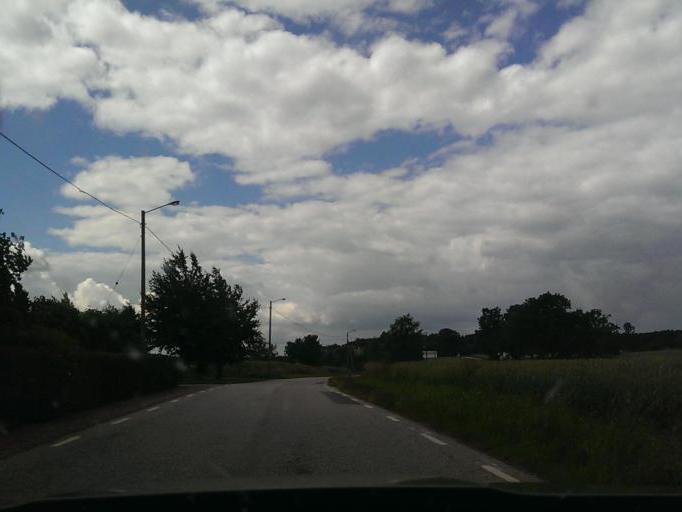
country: SE
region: Skane
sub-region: Eslovs Kommun
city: Eslov
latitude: 55.8918
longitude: 13.3054
